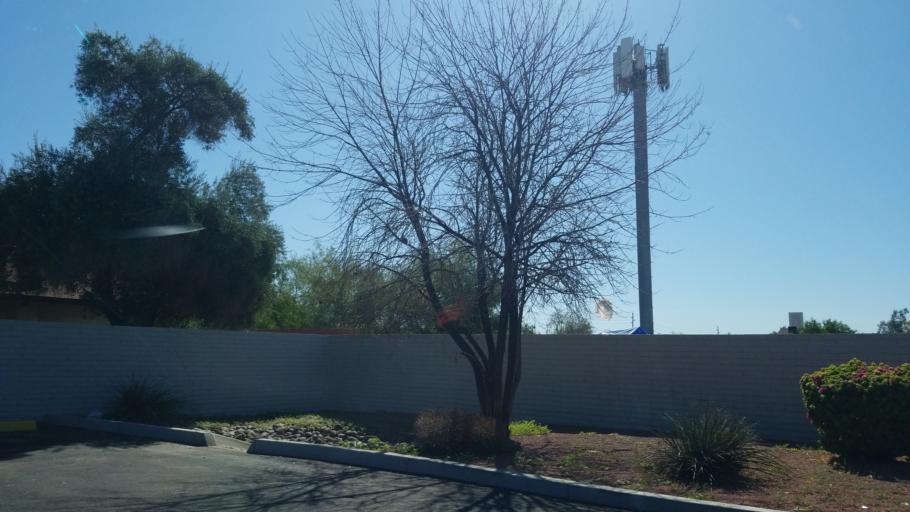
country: US
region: Arizona
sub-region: Maricopa County
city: Glendale
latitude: 33.4799
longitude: -112.1876
